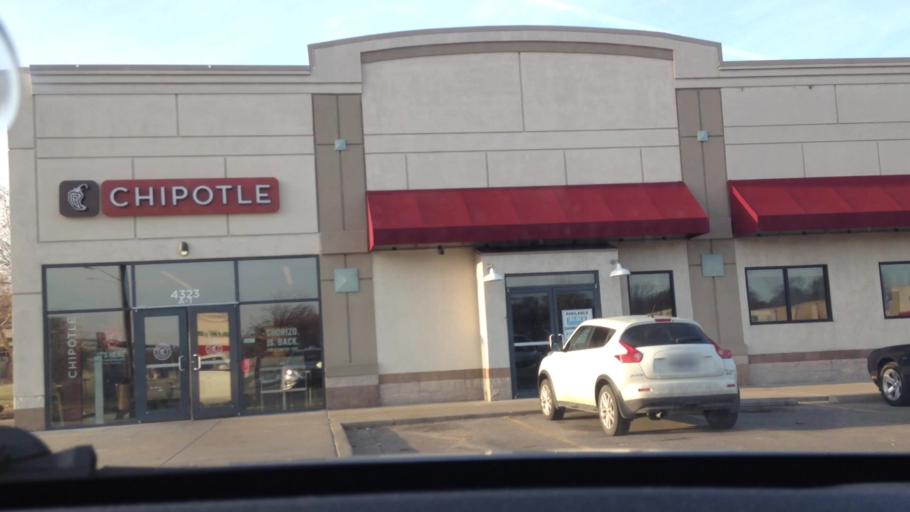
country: US
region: Missouri
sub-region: Clay County
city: Gladstone
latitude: 39.1735
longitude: -94.5354
